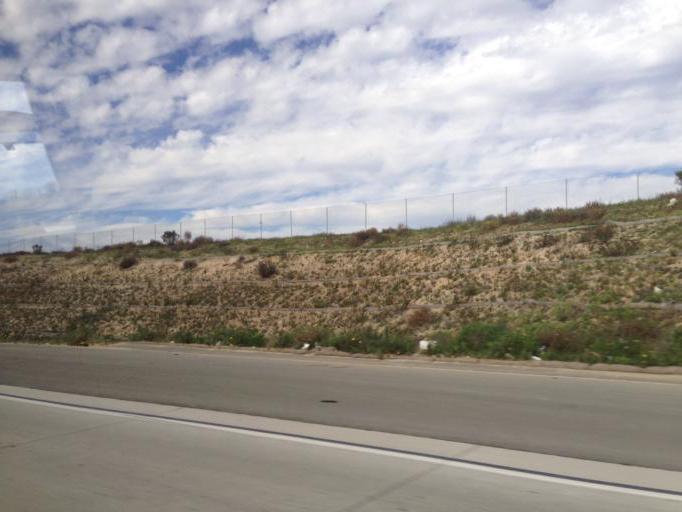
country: MX
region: Baja California
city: Tijuana
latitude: 32.5666
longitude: -117.0067
